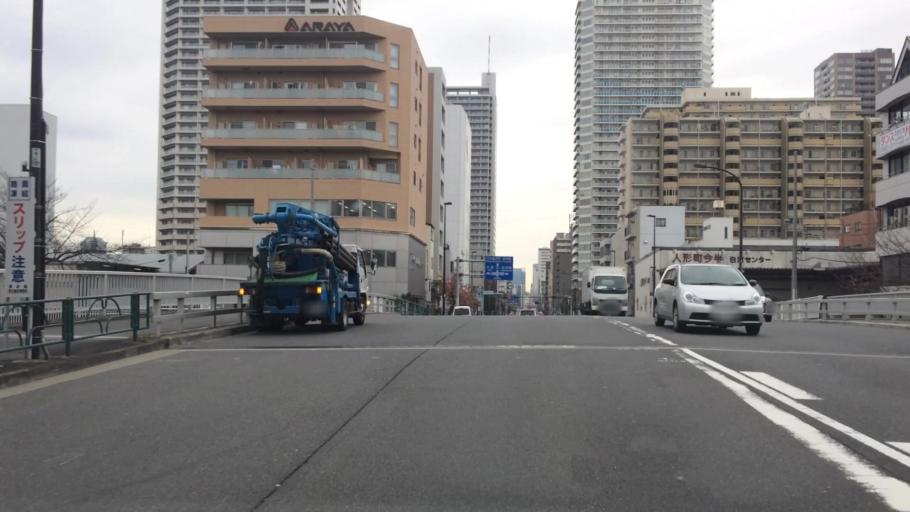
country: JP
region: Tokyo
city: Urayasu
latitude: 35.6827
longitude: 139.8104
